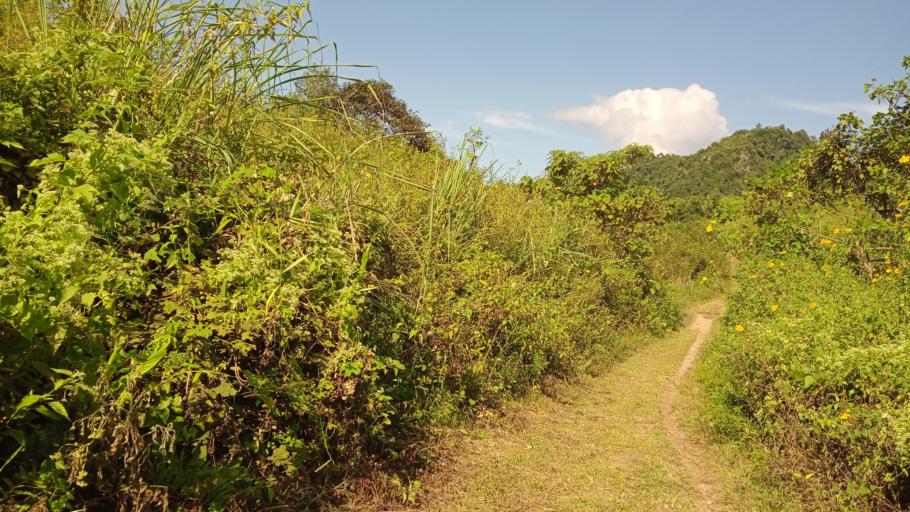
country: LA
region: Xiangkhoang
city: Phonsavan
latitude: 19.1102
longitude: 102.9295
